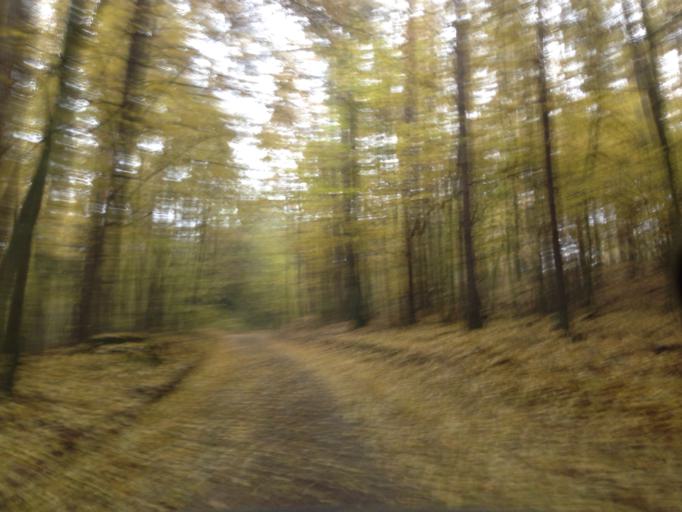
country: PL
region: Kujawsko-Pomorskie
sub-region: Powiat brodnicki
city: Gorzno
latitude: 53.2161
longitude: 19.6936
